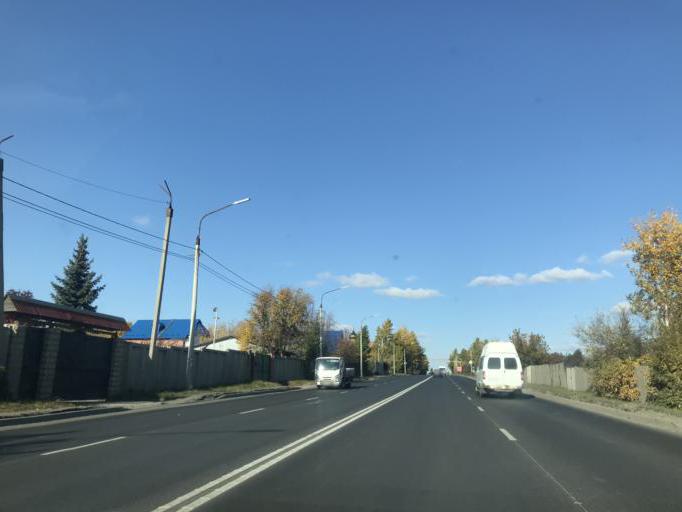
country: RU
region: Chelyabinsk
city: Roshchino
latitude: 55.2359
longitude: 61.3170
